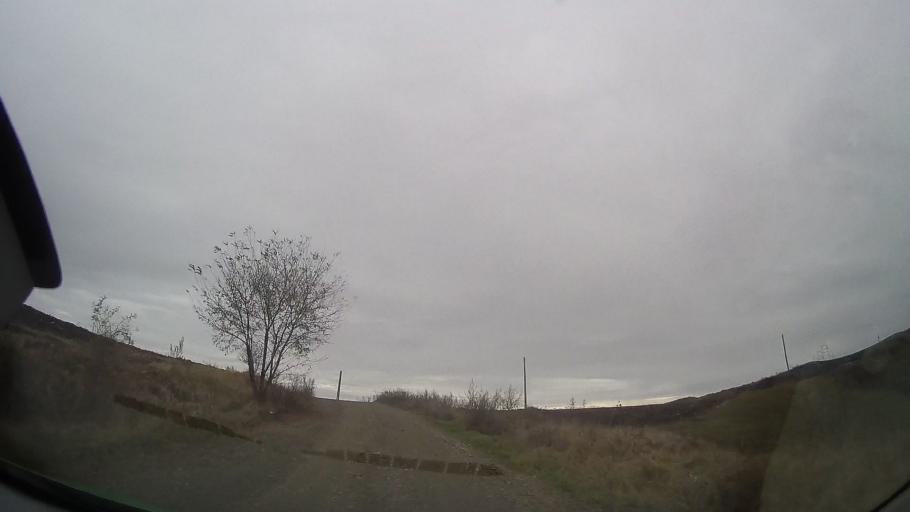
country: RO
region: Mures
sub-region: Comuna Bala
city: Bala
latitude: 46.6995
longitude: 24.4924
